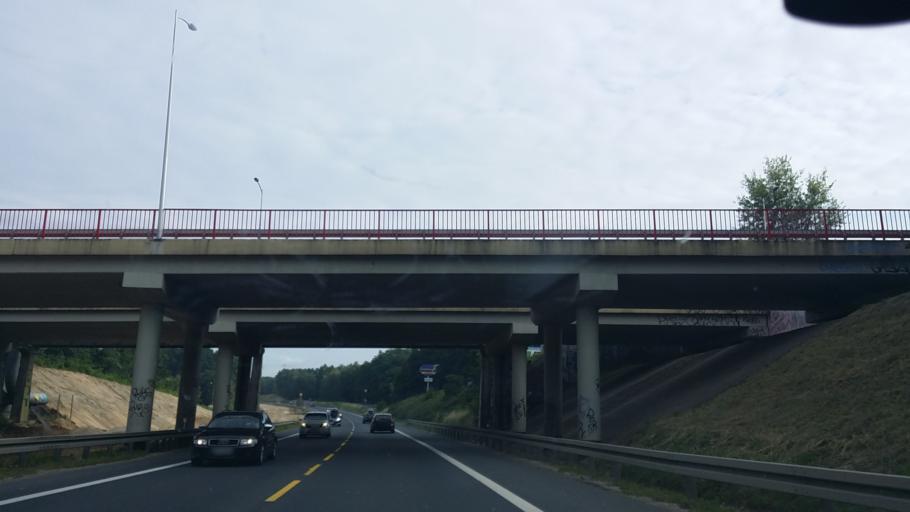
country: PL
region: Lubusz
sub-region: Zielona Gora
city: Zielona Gora
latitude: 51.9388
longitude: 15.5480
